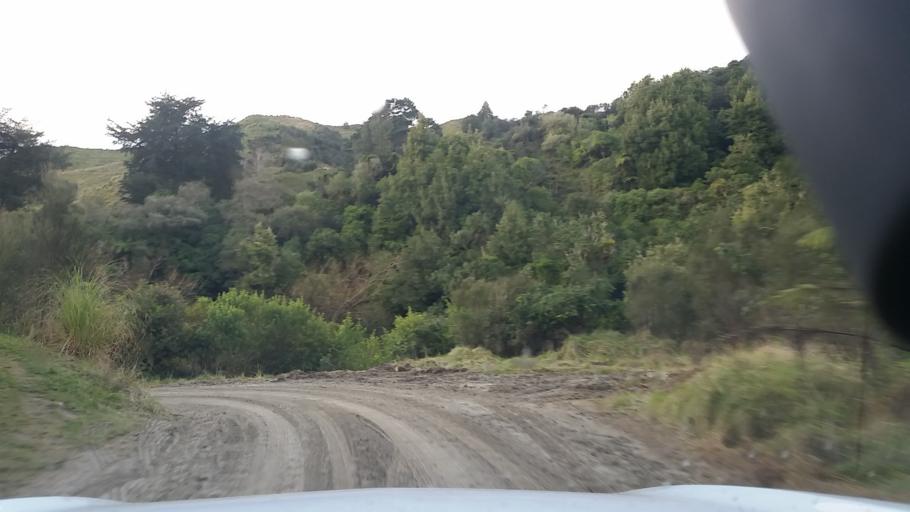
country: NZ
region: Taranaki
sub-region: South Taranaki District
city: Patea
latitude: -39.5658
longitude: 174.8097
